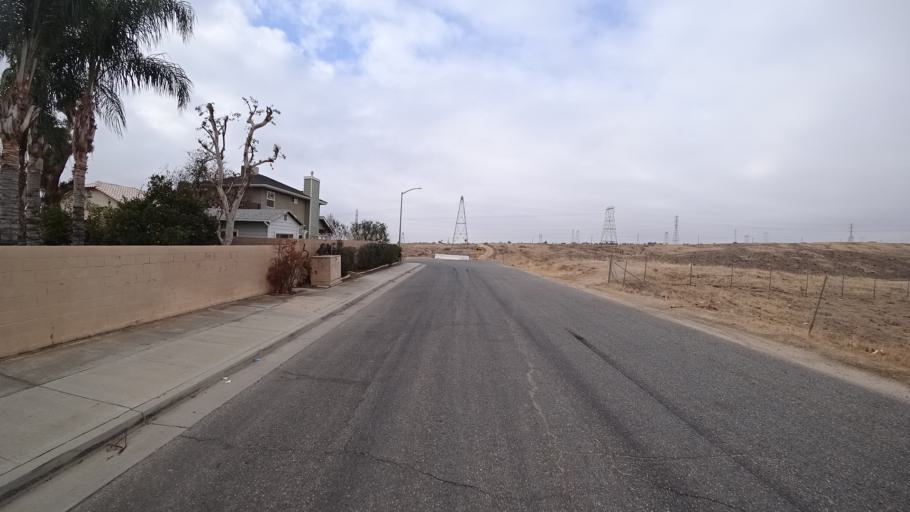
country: US
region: California
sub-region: Kern County
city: Bakersfield
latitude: 35.3833
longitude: -118.9180
